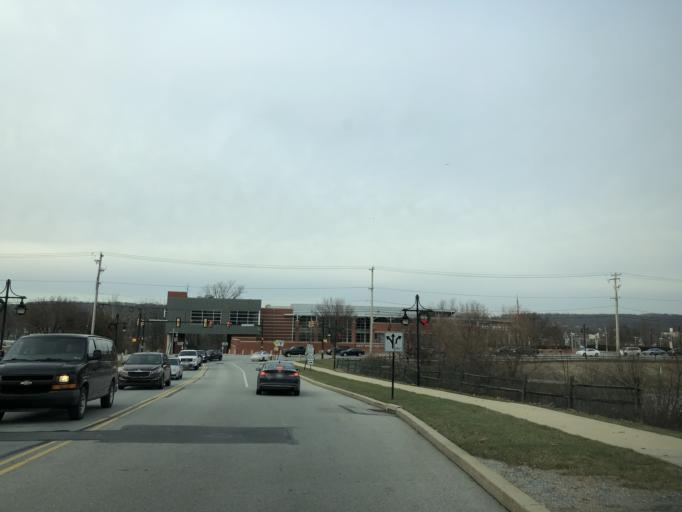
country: US
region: Pennsylvania
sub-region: Chester County
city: Exton
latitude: 40.0243
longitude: -75.6289
